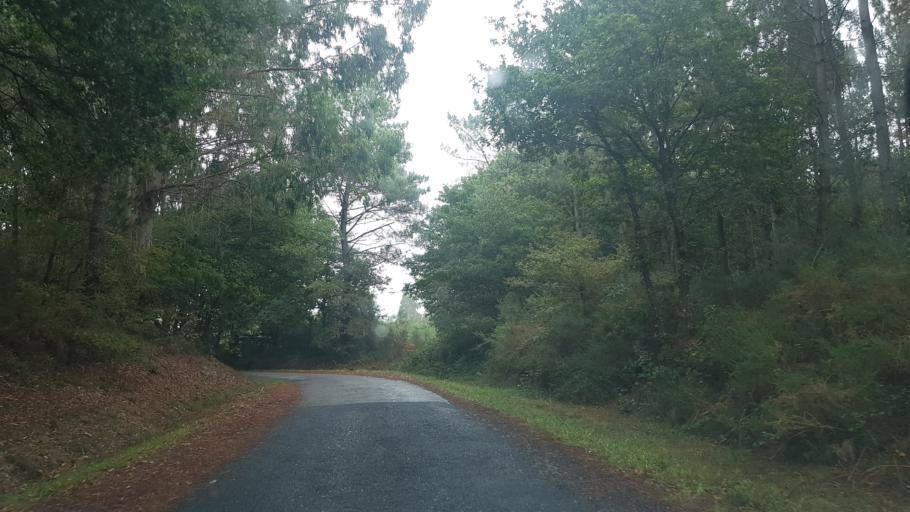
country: ES
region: Galicia
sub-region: Provincia de Lugo
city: Friol
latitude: 43.1272
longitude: -7.8135
